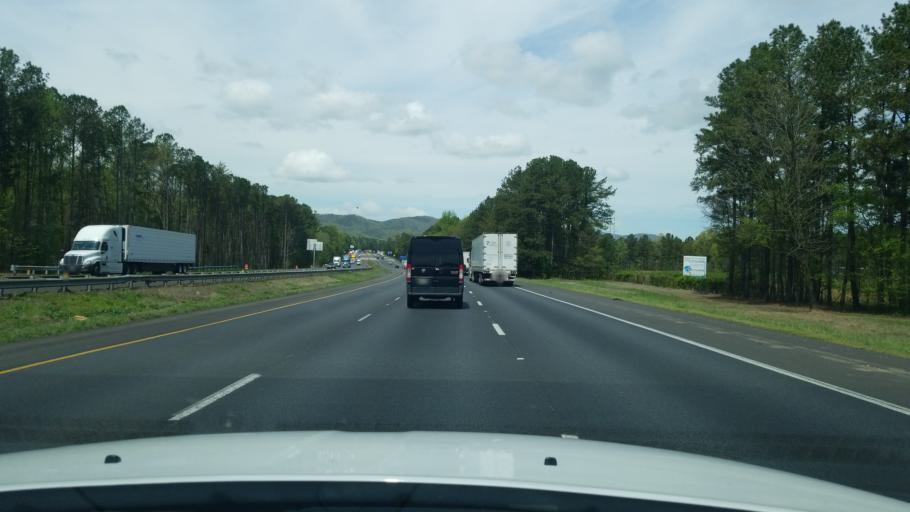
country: US
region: Georgia
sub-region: Whitfield County
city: Dalton
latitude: 34.6617
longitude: -84.9877
